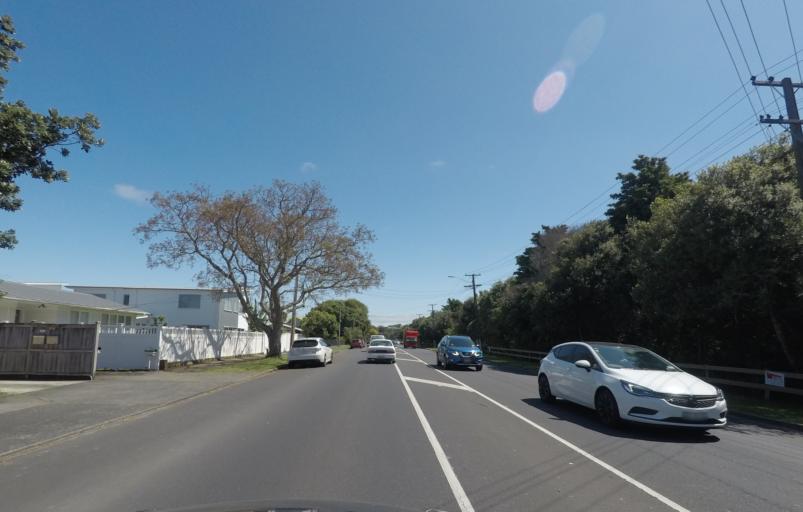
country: NZ
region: Auckland
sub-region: Auckland
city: Tamaki
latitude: -36.8870
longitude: 174.8235
